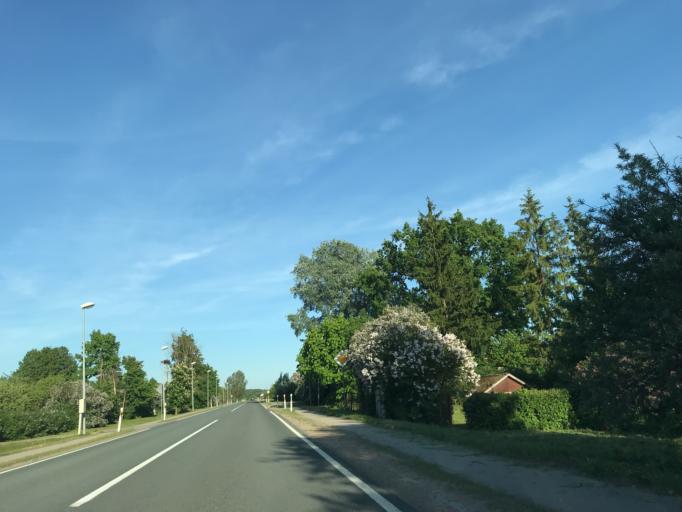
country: LV
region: Olaine
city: Olaine
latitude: 56.6274
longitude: 23.9396
